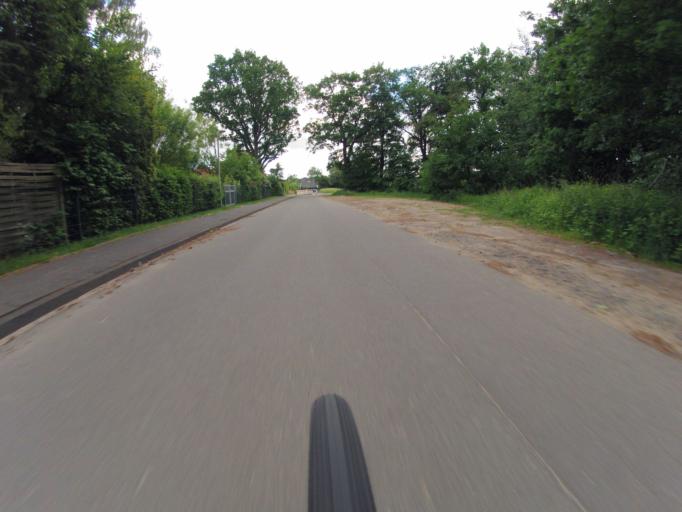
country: DE
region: North Rhine-Westphalia
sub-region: Regierungsbezirk Munster
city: Birgte
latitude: 52.2946
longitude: 7.6482
